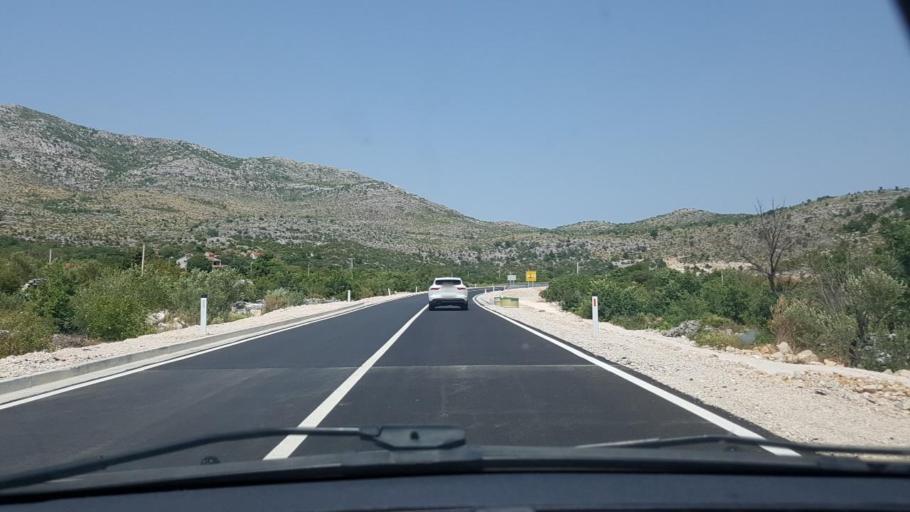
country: HR
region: Dubrovacko-Neretvanska
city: Podgora
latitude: 42.9480
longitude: 17.7781
